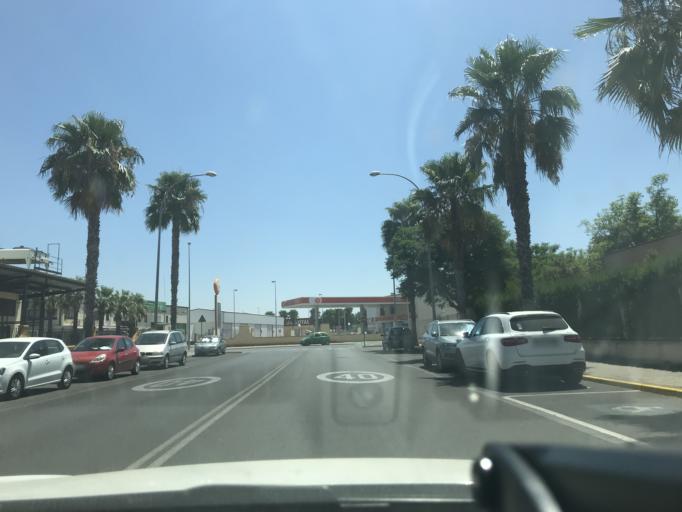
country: ES
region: Andalusia
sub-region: Provincia de Sevilla
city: La Rinconada
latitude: 37.4873
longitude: -5.9356
